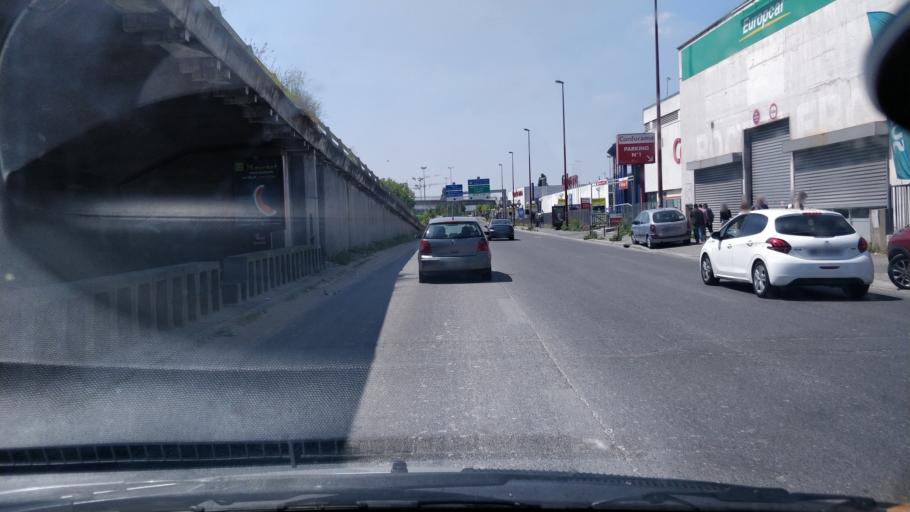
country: FR
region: Ile-de-France
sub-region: Departement de Seine-Saint-Denis
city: Bondy
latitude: 48.9059
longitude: 2.4796
